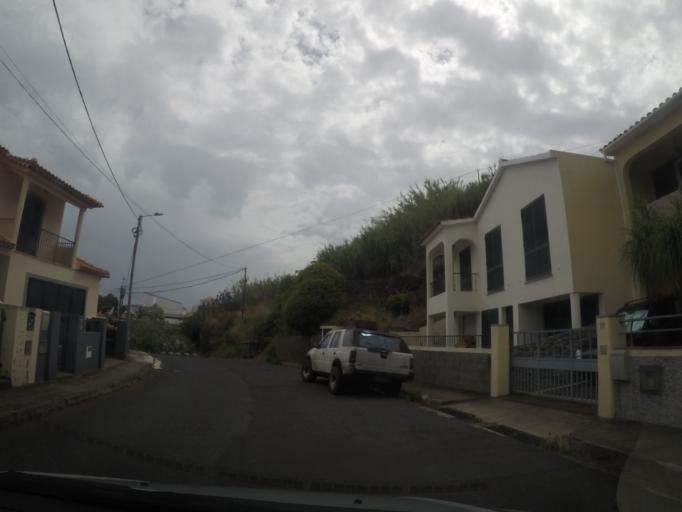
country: PT
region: Madeira
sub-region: Santa Cruz
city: Santa Cruz
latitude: 32.6765
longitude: -16.8110
